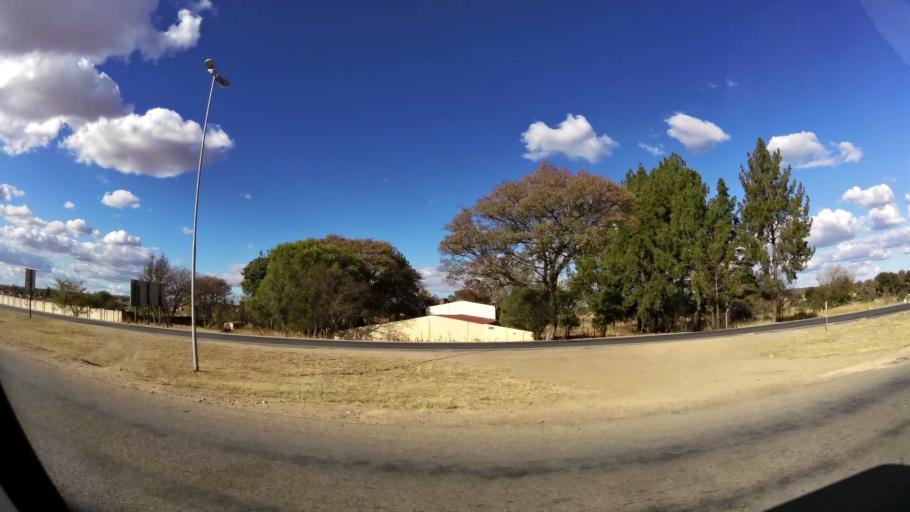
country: ZA
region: Limpopo
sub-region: Capricorn District Municipality
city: Polokwane
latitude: -23.9389
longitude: 29.4489
